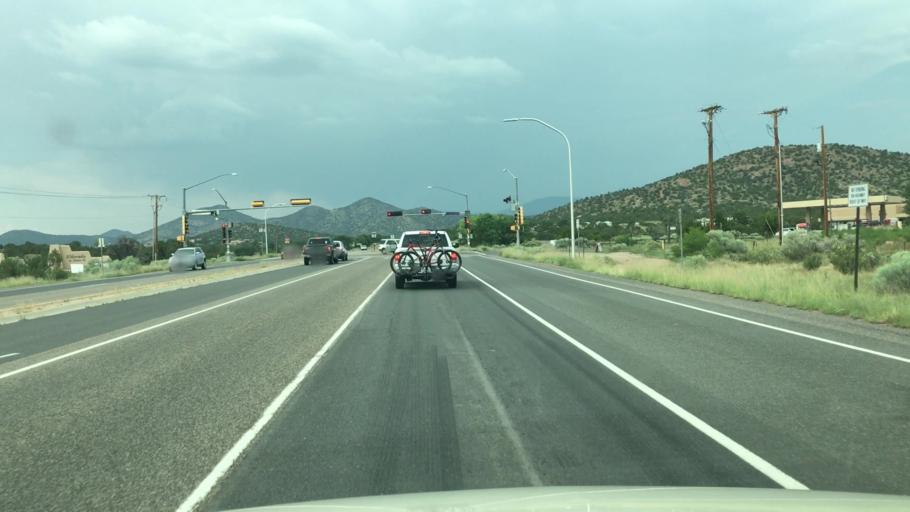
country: US
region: New Mexico
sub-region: Santa Fe County
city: Eldorado at Santa Fe
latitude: 35.5359
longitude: -105.8872
